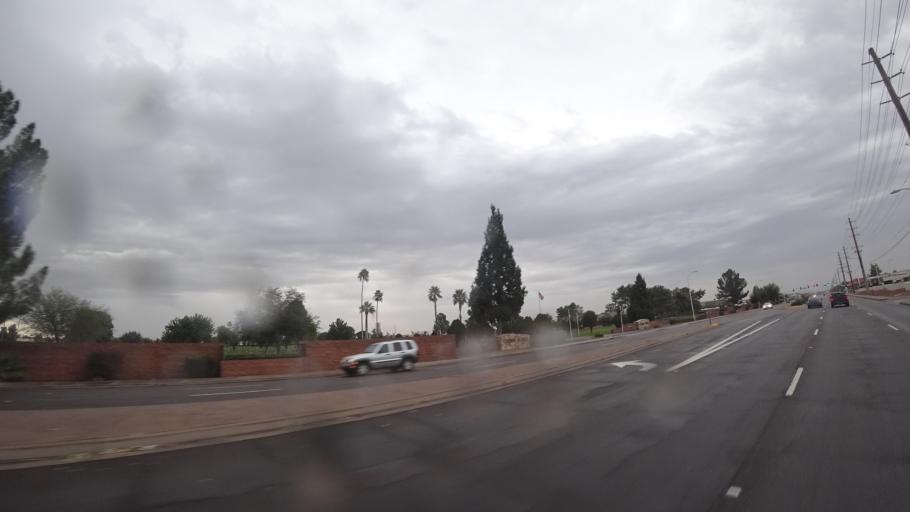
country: US
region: Arizona
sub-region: Maricopa County
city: Tempe
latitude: 33.4538
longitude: -111.9093
